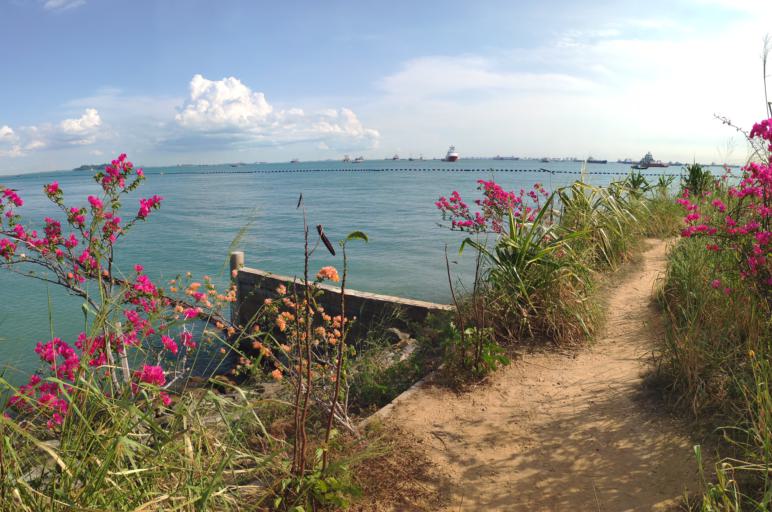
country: SG
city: Singapore
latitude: 1.2473
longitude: 103.8226
